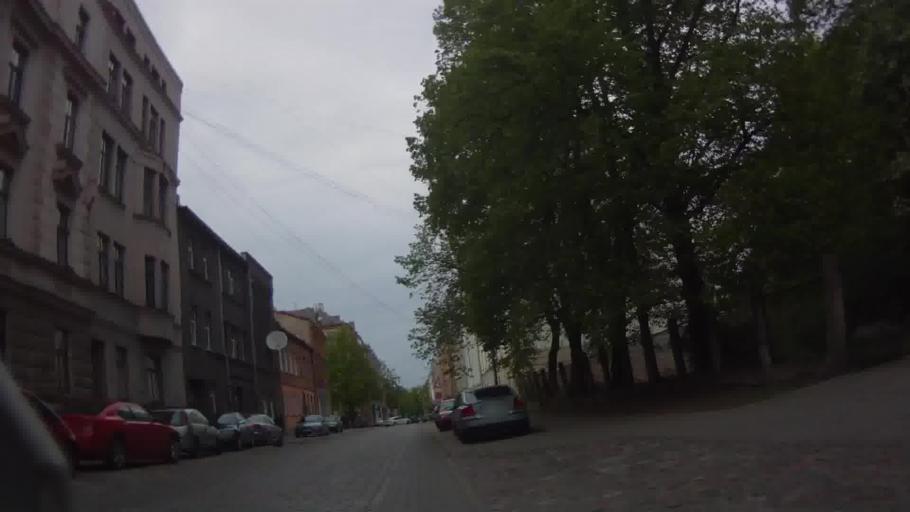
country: LV
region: Riga
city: Riga
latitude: 56.9723
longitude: 24.1372
